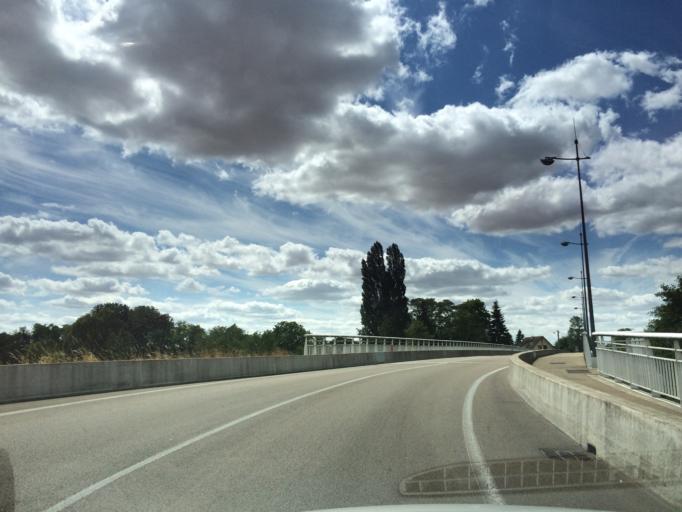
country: FR
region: Bourgogne
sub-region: Departement de l'Yonne
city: Migennes
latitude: 47.9567
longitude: 3.5026
